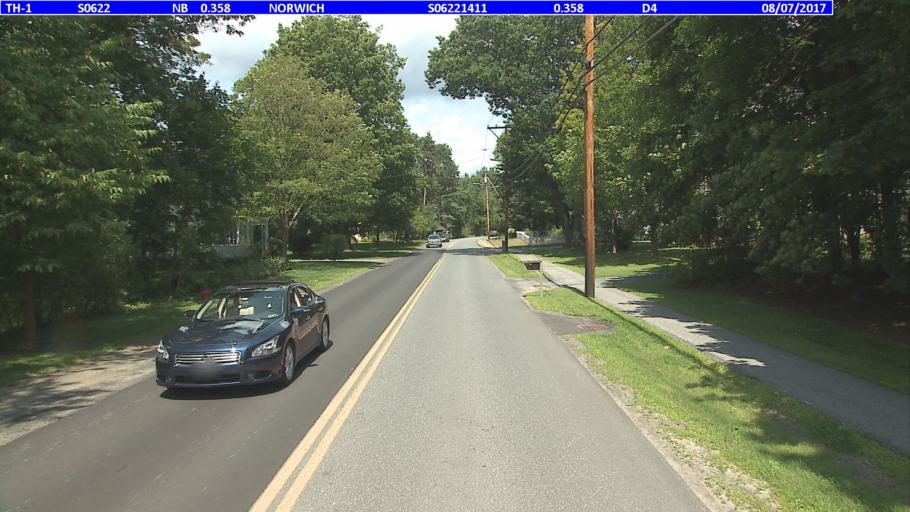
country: US
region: New Hampshire
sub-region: Grafton County
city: Hanover
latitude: 43.7184
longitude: -72.3093
